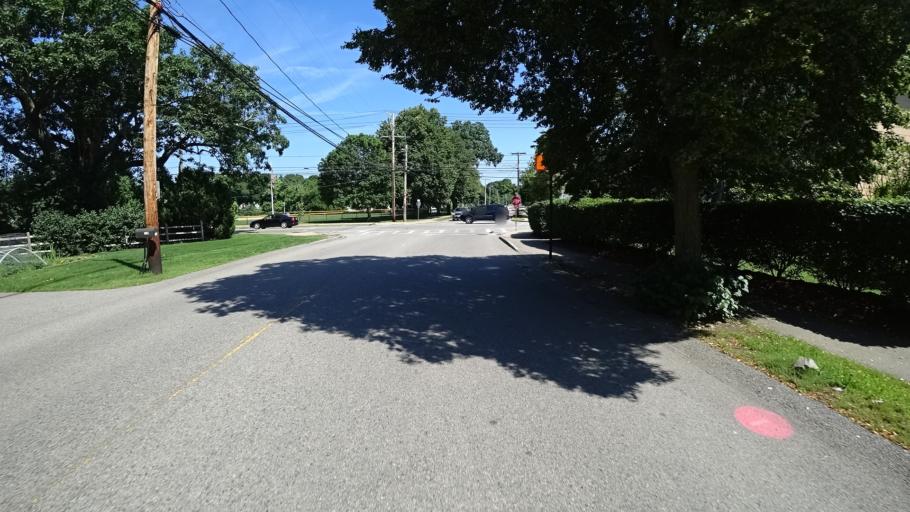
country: US
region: Massachusetts
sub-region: Norfolk County
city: Dedham
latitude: 42.2445
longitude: -71.1634
